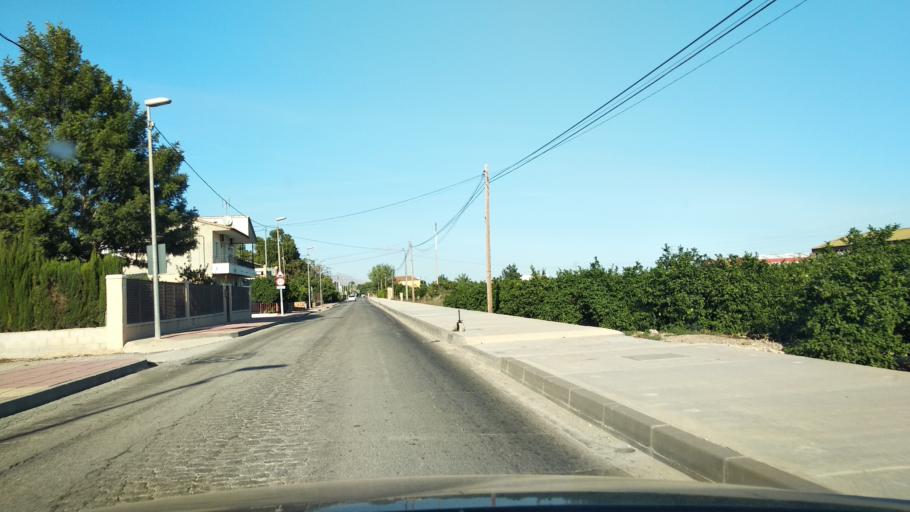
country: ES
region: Murcia
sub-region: Murcia
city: Santomera
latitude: 38.0410
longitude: -1.0456
